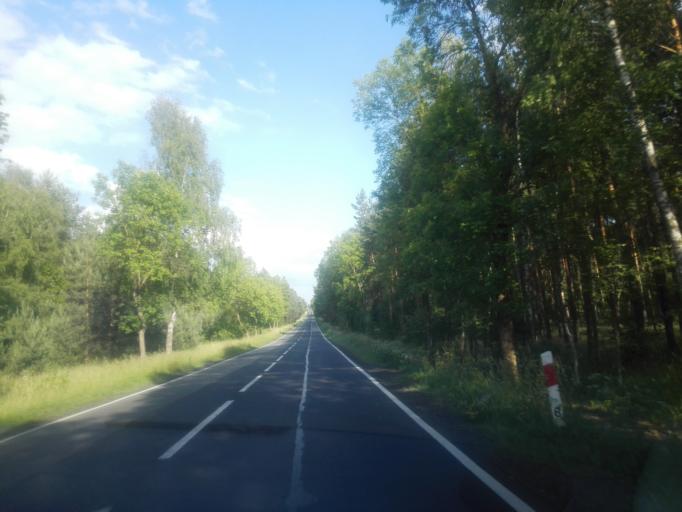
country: PL
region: Silesian Voivodeship
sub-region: Powiat czestochowski
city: Potok Zloty
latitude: 50.7268
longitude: 19.4141
